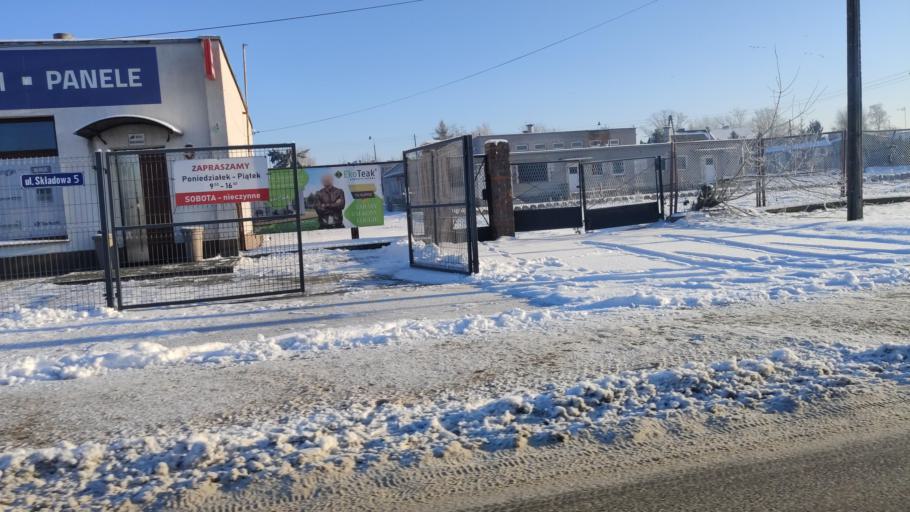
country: PL
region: Kujawsko-Pomorskie
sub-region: Powiat zninski
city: Znin
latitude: 52.8482
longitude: 17.7422
